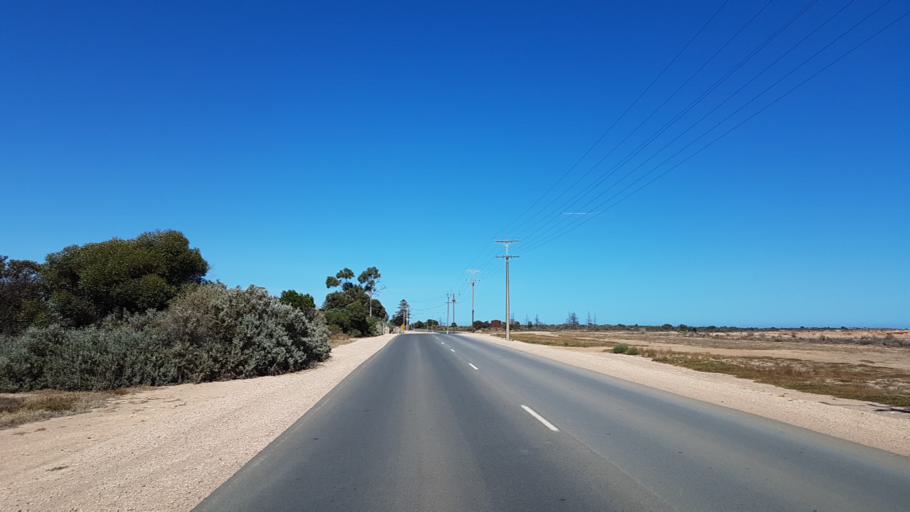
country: AU
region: South Australia
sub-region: Copper Coast
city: Wallaroo
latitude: -33.9340
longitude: 137.6103
